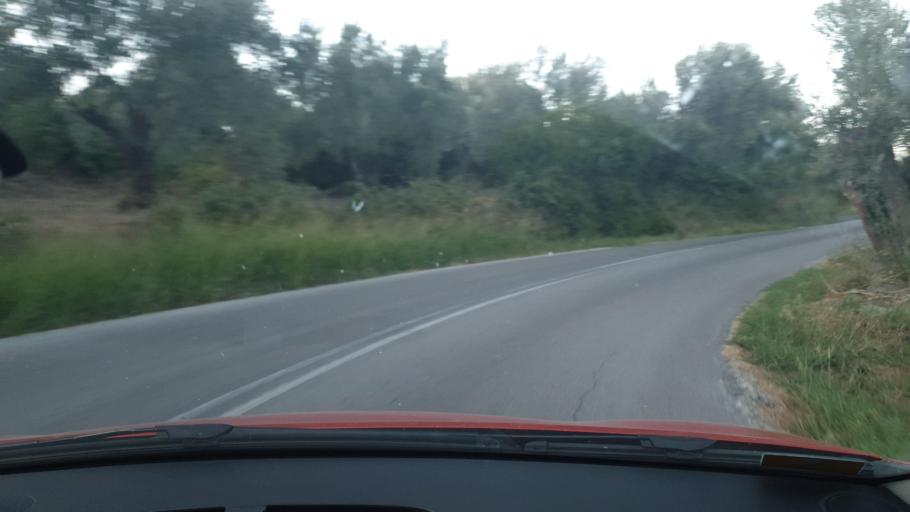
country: GR
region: Central Greece
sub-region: Nomos Evvoias
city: Kymi
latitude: 38.6295
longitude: 24.1166
